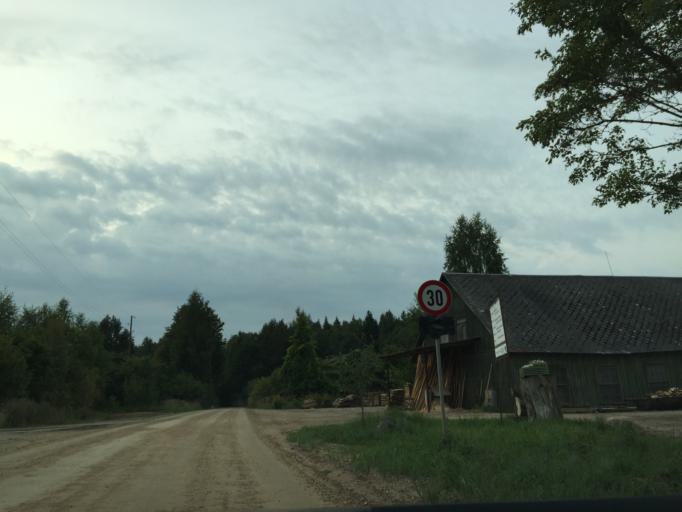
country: LV
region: Ogre
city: Ogre
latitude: 56.8246
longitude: 24.6556
